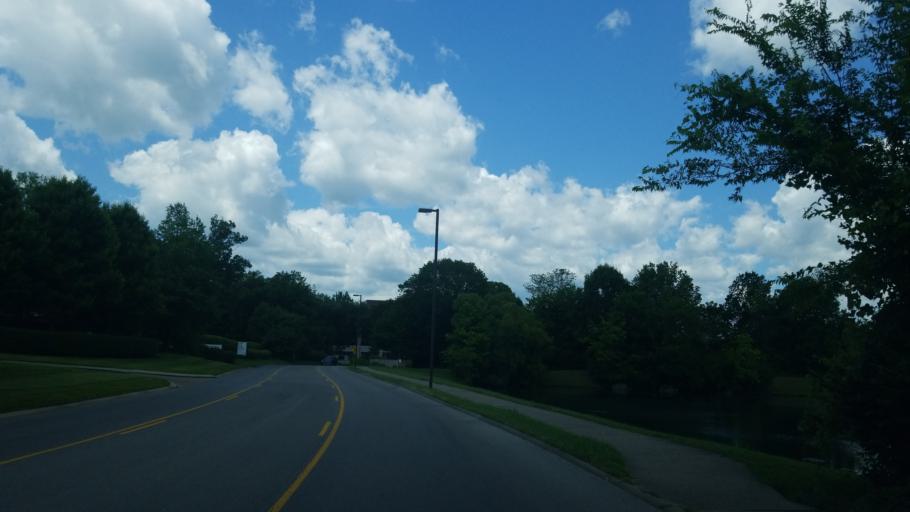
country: US
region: Tennessee
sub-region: Williamson County
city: Brentwood
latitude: 36.0330
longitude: -86.8099
